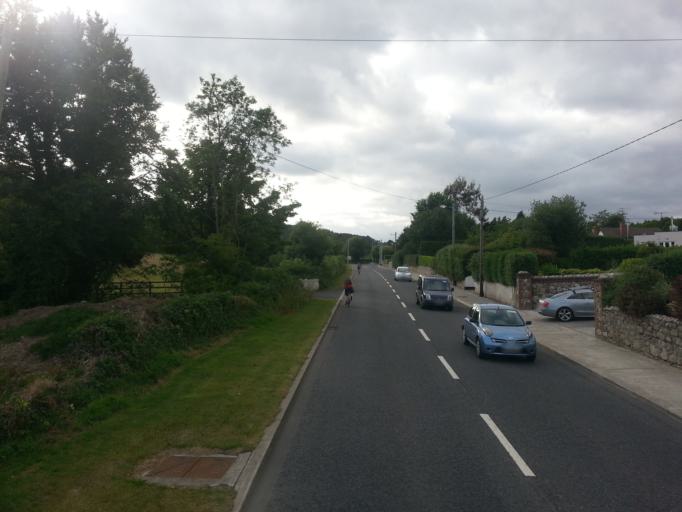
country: IE
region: Leinster
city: Sandyford
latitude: 53.2497
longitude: -6.2078
